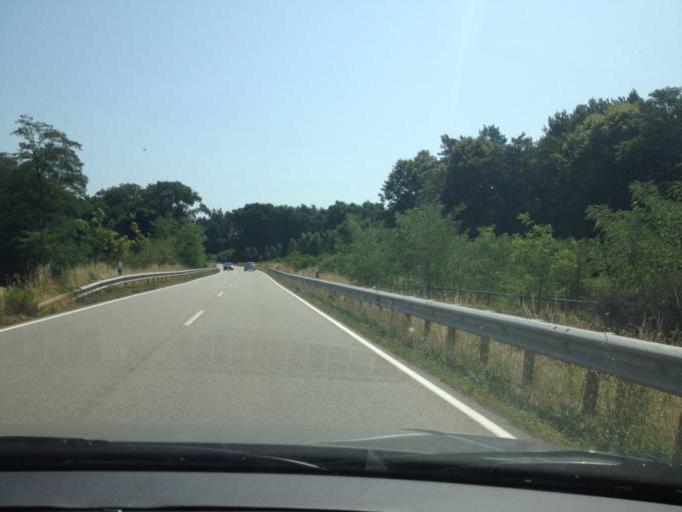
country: DE
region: Rheinland-Pfalz
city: Gries
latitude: 49.4098
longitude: 7.4056
